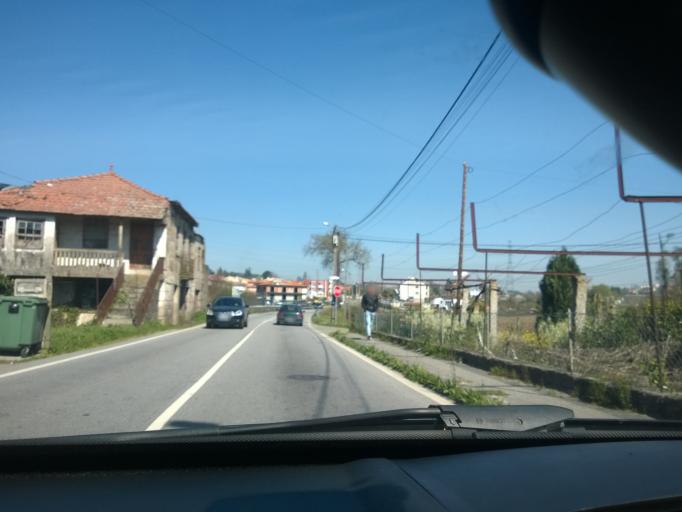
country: PT
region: Porto
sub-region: Paredes
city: Paredes
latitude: 41.1738
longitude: -8.3060
